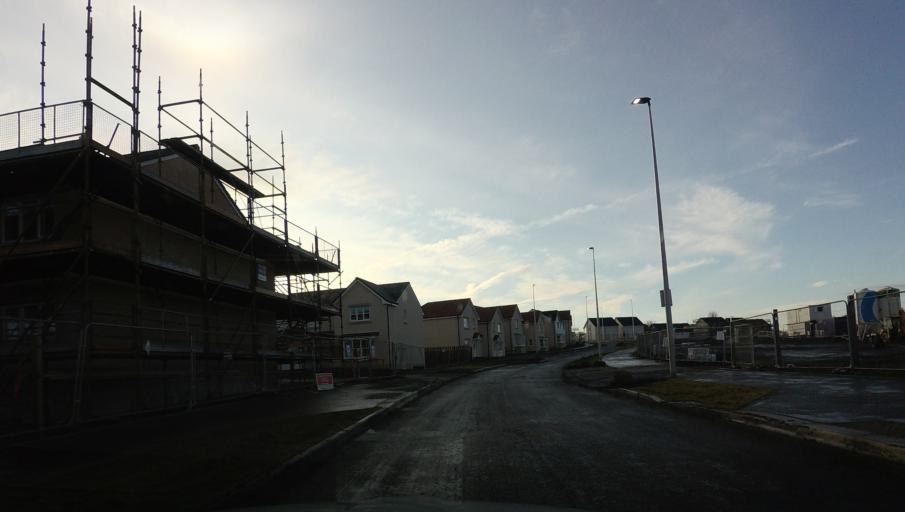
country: GB
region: Scotland
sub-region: West Lothian
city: East Calder
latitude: 55.9009
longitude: -3.4428
